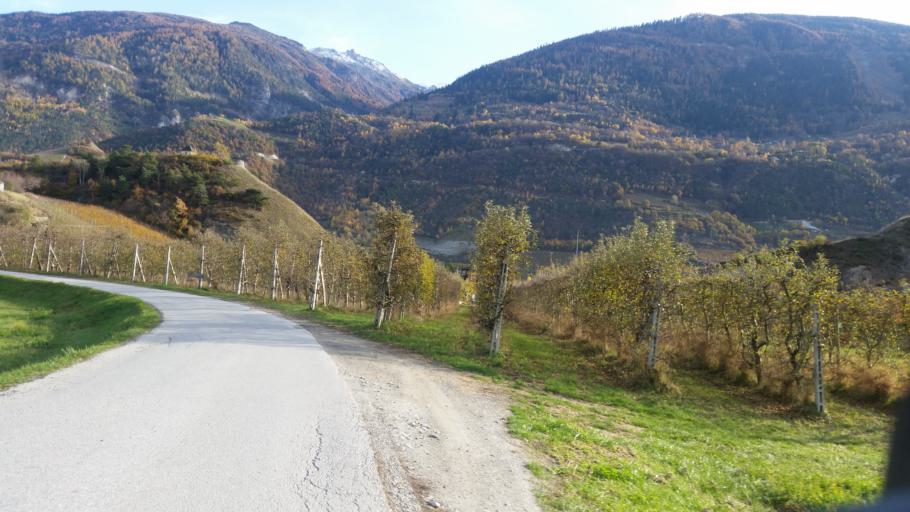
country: CH
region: Valais
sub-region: Sierre District
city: Grone
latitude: 46.2634
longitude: 7.4736
